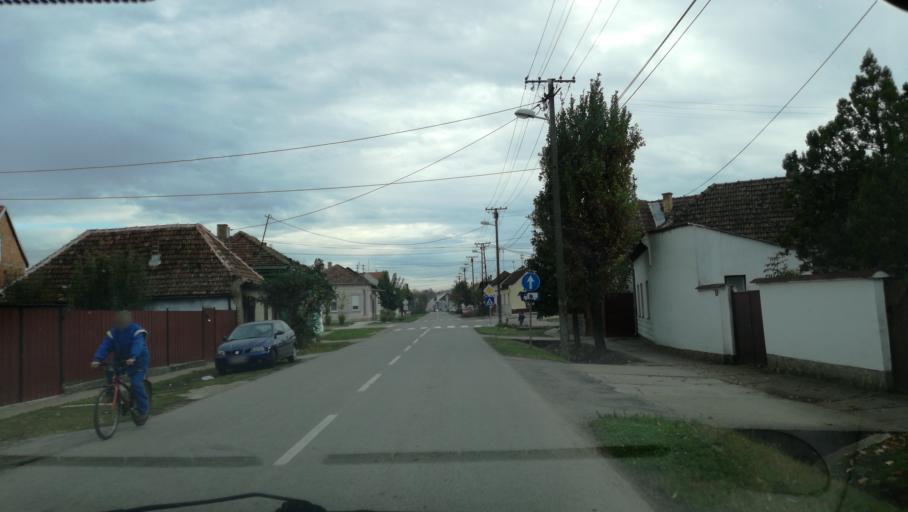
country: RS
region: Autonomna Pokrajina Vojvodina
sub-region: Severnobanatski Okrug
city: Kikinda
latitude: 45.8385
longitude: 20.4692
